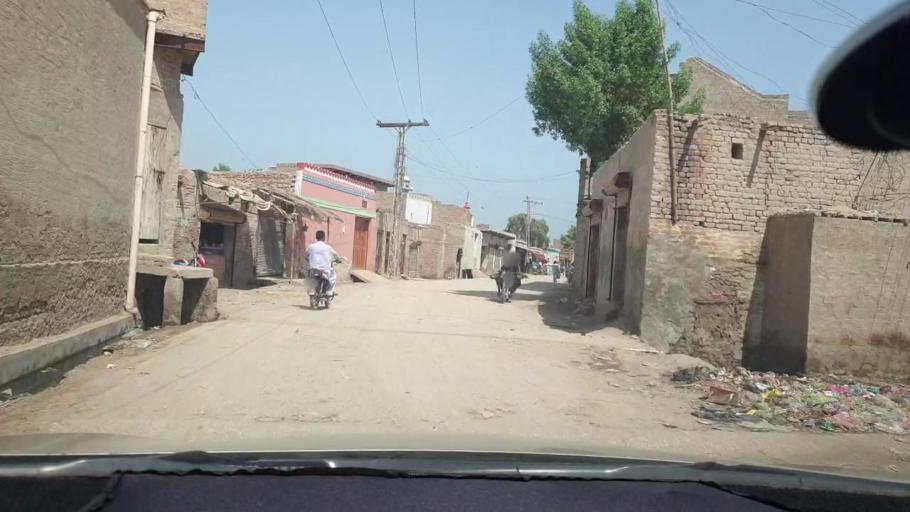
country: PK
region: Sindh
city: Kambar
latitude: 27.5851
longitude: 67.9979
